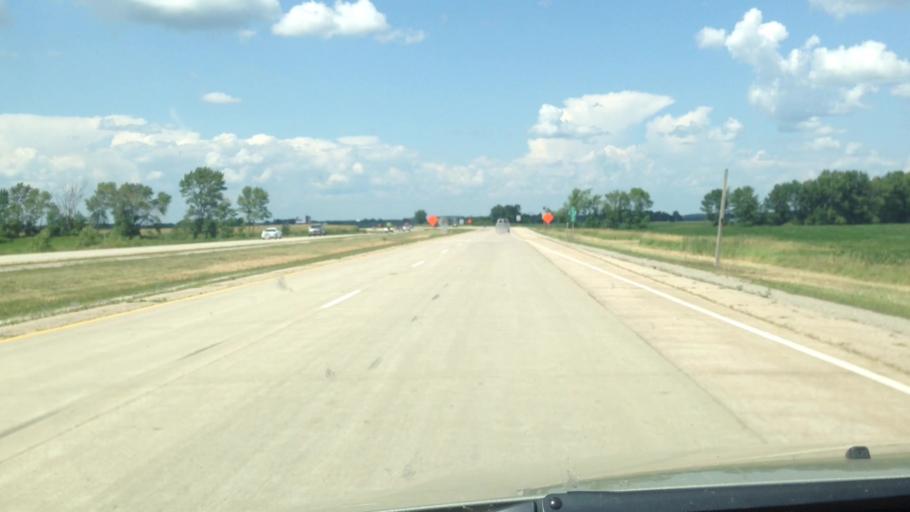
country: US
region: Wisconsin
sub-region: Brown County
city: Pulaski
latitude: 44.6794
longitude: -88.3109
